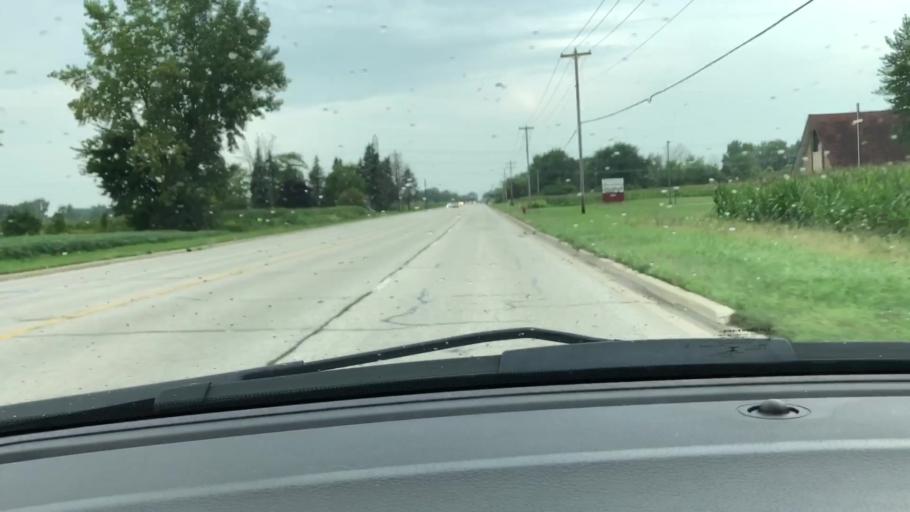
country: US
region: Michigan
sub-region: Saginaw County
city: Carrollton
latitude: 43.4805
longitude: -84.0066
